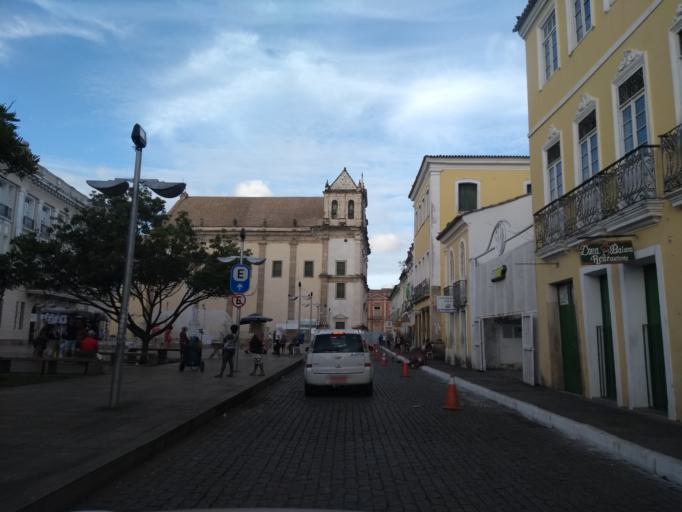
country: BR
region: Bahia
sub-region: Salvador
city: Salvador
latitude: -12.9735
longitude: -38.5109
